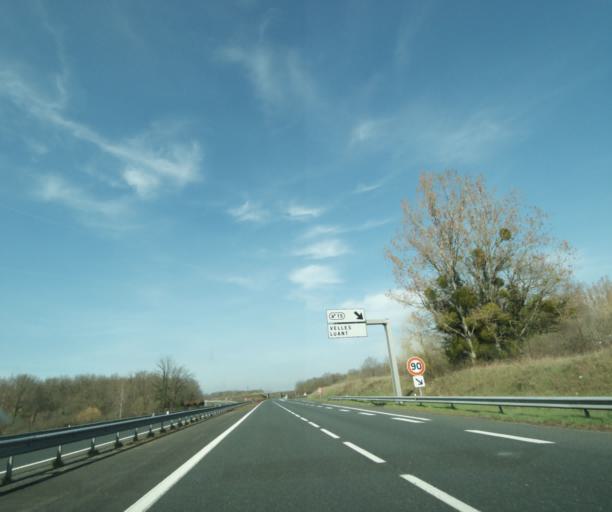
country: FR
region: Centre
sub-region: Departement de l'Indre
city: Luant
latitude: 46.6956
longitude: 1.5838
